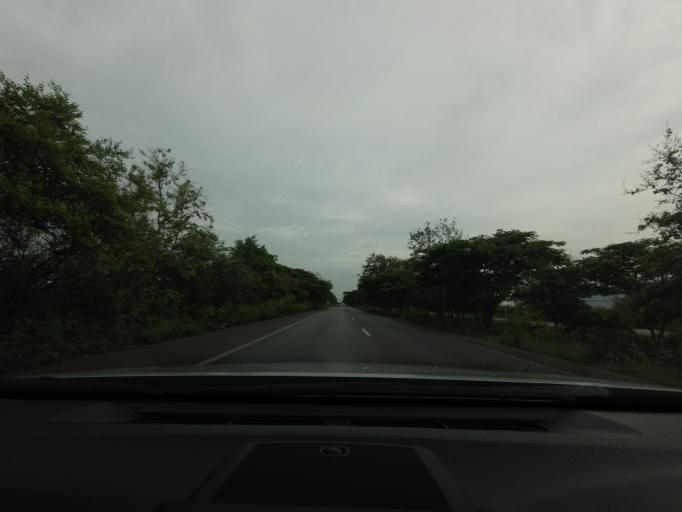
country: TH
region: Phetchaburi
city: Cha-am
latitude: 12.7672
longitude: 99.9350
